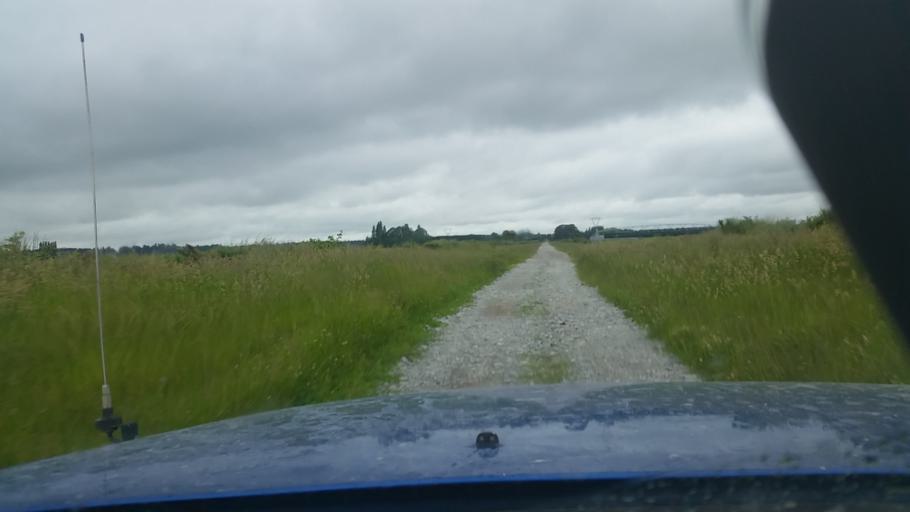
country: NZ
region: Canterbury
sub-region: Ashburton District
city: Ashburton
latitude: -43.8431
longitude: 171.6772
